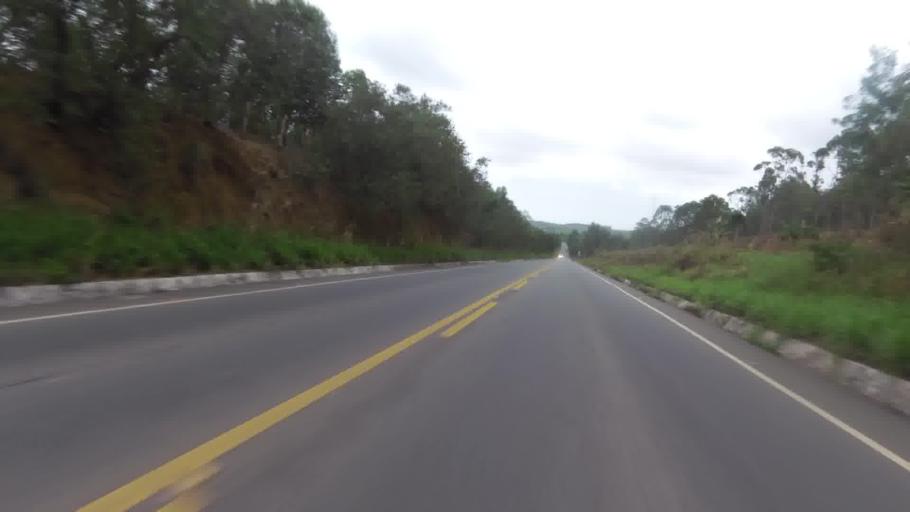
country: BR
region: Espirito Santo
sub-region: Piuma
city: Piuma
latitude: -20.7913
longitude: -40.7512
